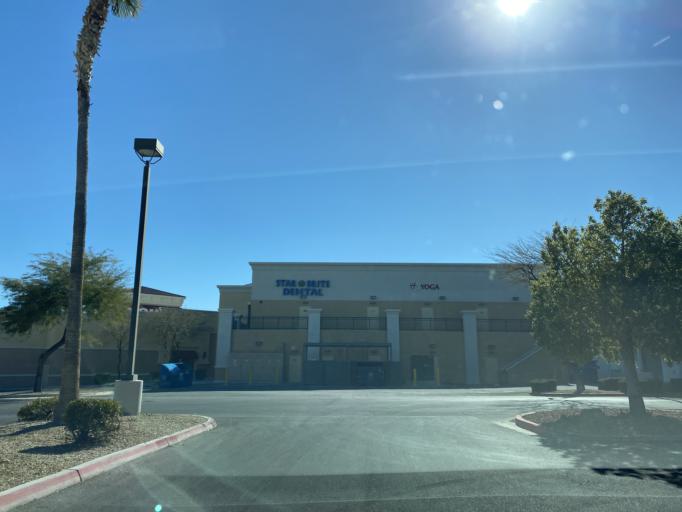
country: US
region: Nevada
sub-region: Clark County
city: Summerlin South
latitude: 36.2841
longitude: -115.2856
